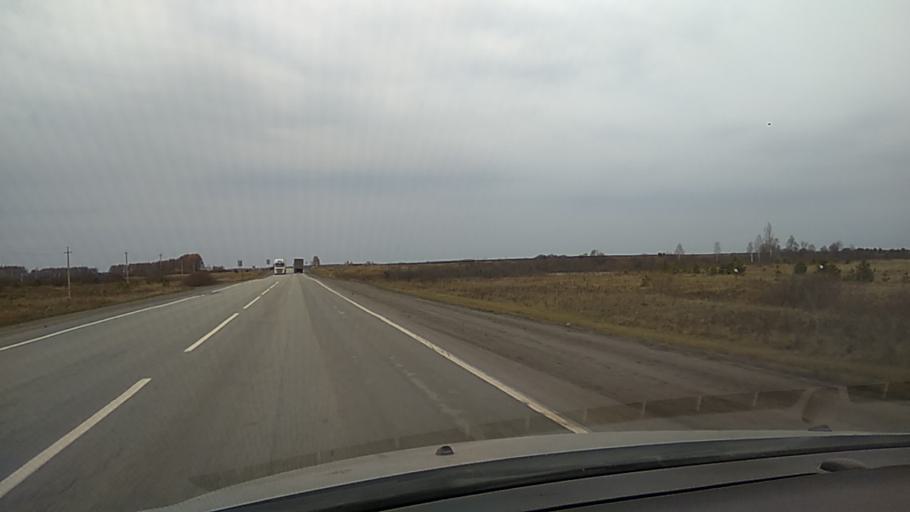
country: RU
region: Sverdlovsk
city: Pyshma
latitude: 57.0463
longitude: 63.4621
